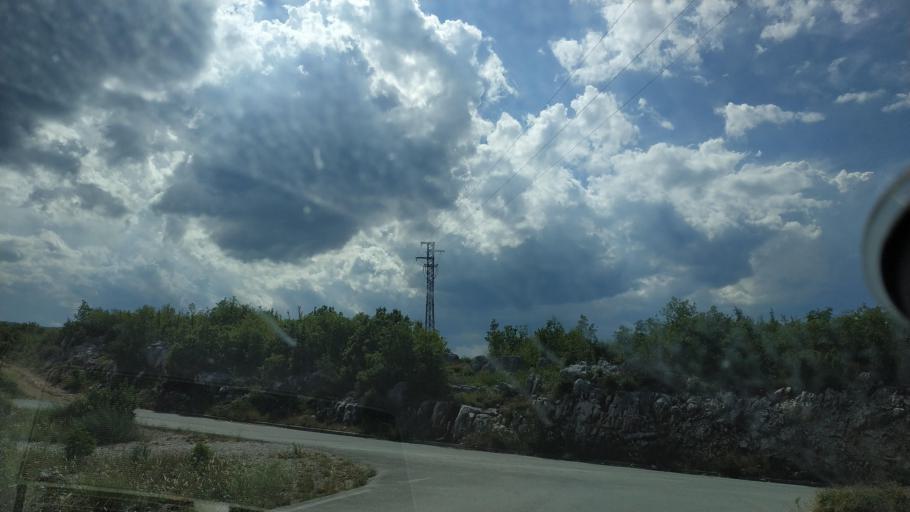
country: HR
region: Splitsko-Dalmatinska
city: Dugopolje
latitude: 43.5812
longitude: 16.6517
